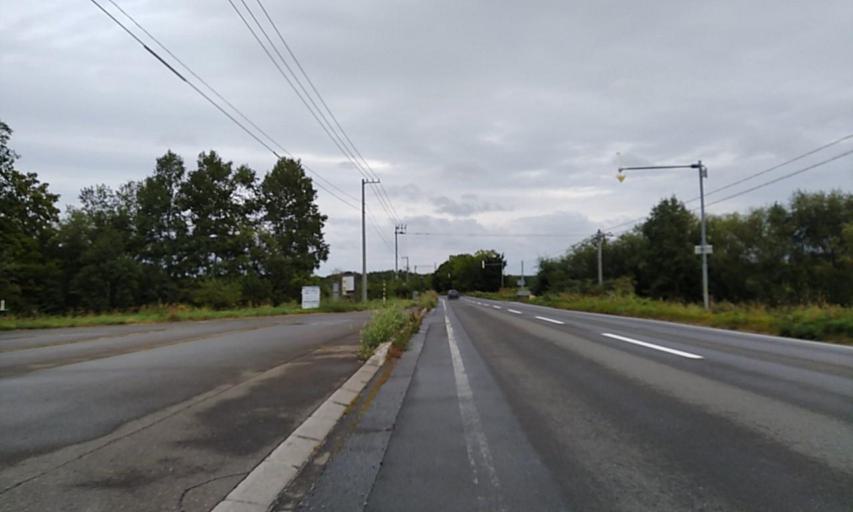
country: JP
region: Hokkaido
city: Kitami
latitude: 44.0877
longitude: 143.9529
